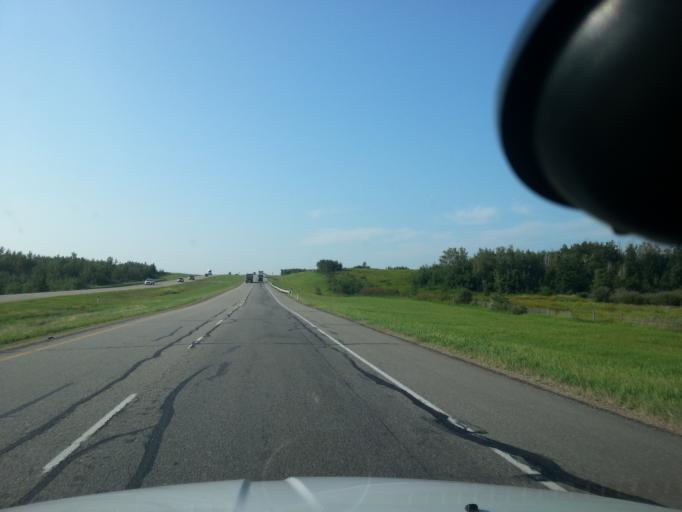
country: CA
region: Alberta
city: Millet
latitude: 53.0629
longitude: -113.5984
